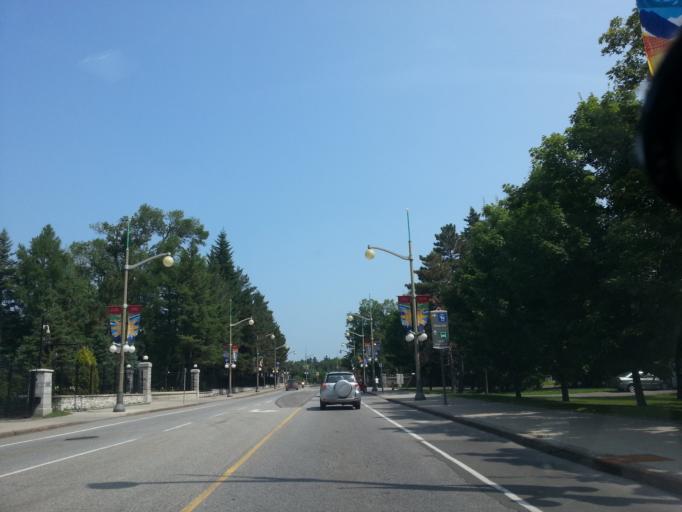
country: CA
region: Ontario
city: Ottawa
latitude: 45.4433
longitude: -75.6934
